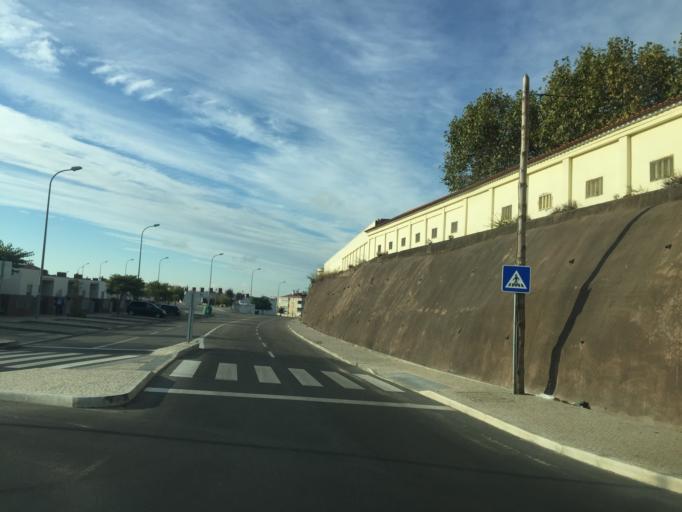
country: PT
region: Lisbon
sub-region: Odivelas
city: Olival do Basto
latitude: 38.7873
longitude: -9.1497
